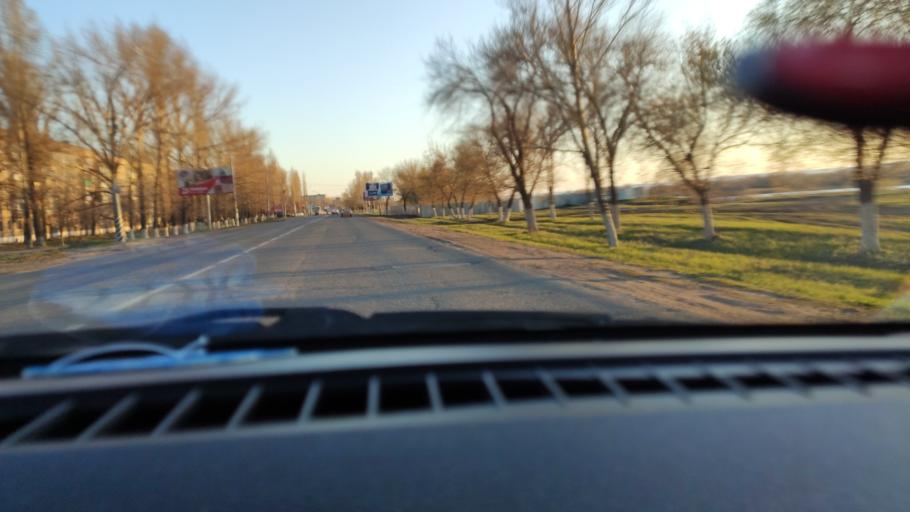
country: RU
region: Saratov
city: Engel's
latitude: 51.4539
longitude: 46.0850
